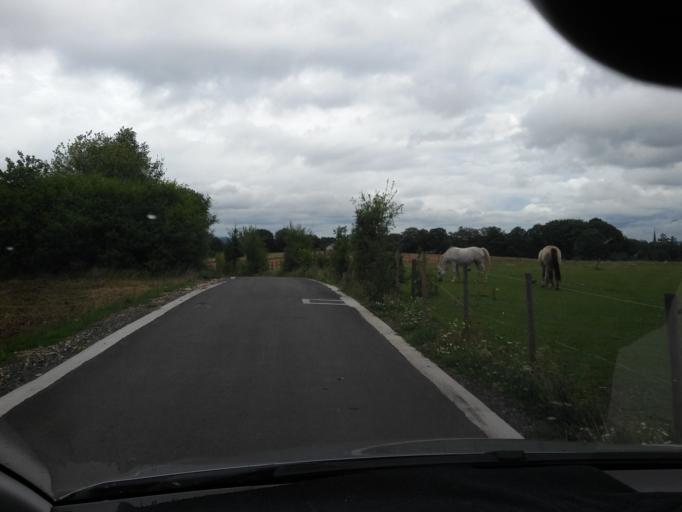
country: BE
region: Wallonia
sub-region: Province du Luxembourg
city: Attert
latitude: 49.7246
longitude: 5.8011
